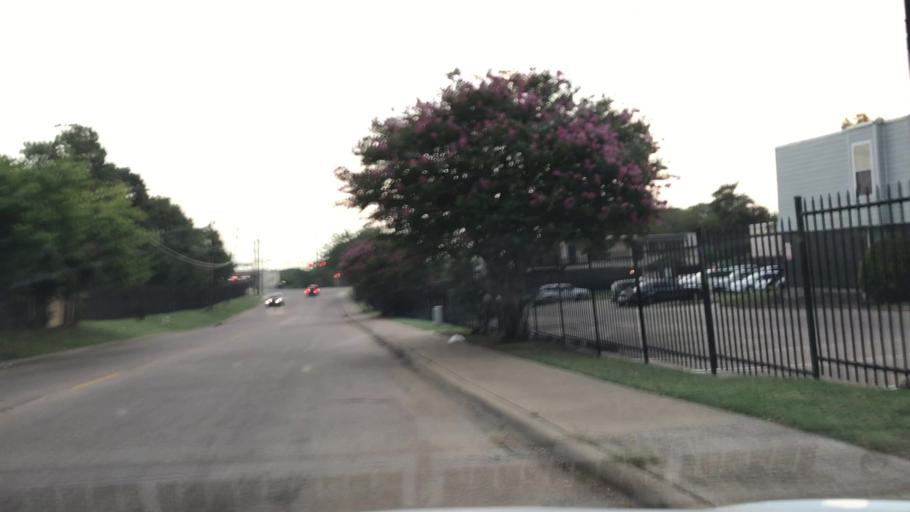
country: US
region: Texas
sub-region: Dallas County
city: Highland Park
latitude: 32.7910
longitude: -96.7123
